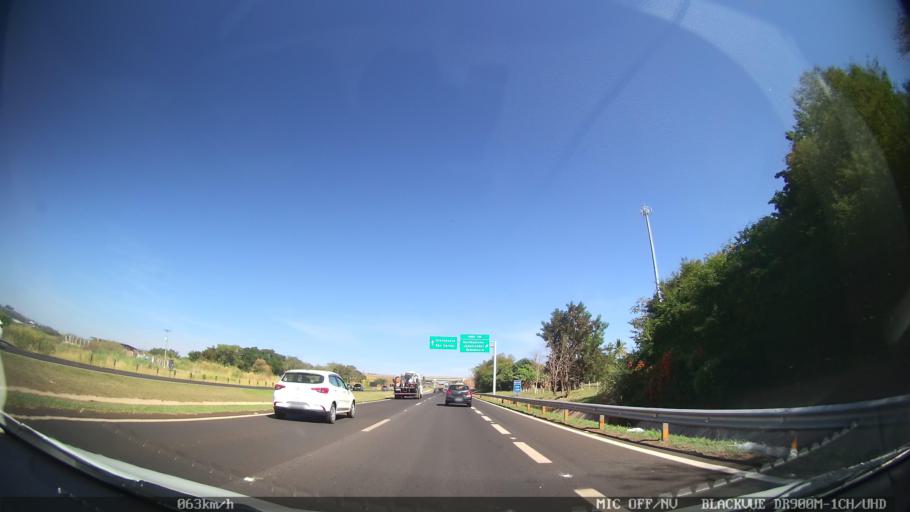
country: BR
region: Sao Paulo
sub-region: Ribeirao Preto
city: Ribeirao Preto
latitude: -21.2193
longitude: -47.7751
